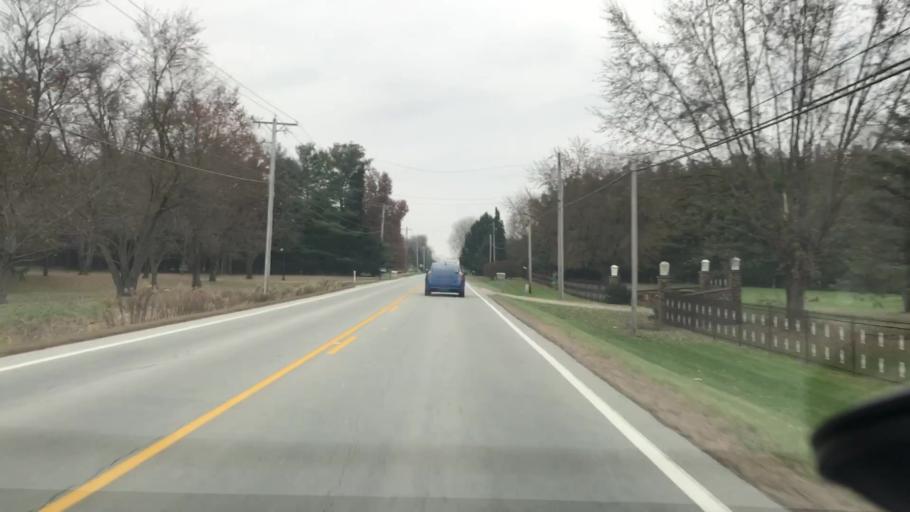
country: US
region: Ohio
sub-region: Clark County
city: Holiday Valley
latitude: 39.7902
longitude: -83.9577
